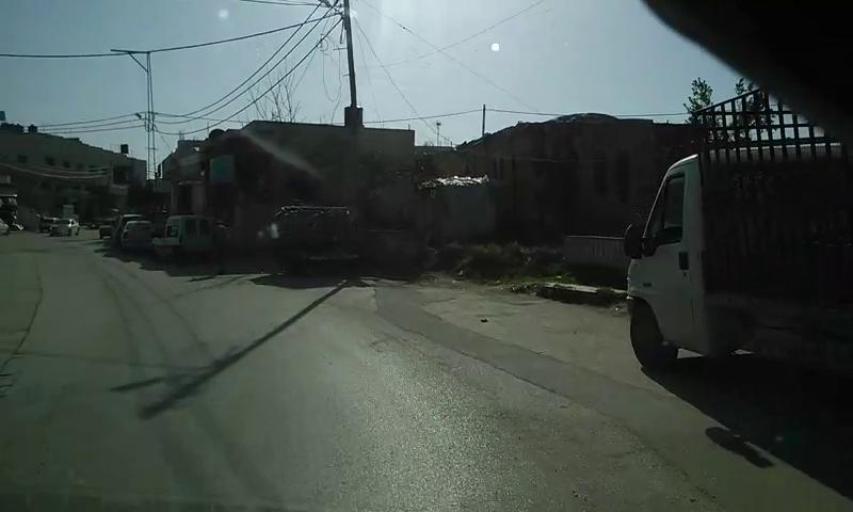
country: PS
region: West Bank
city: Yuta
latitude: 31.4520
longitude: 35.0955
